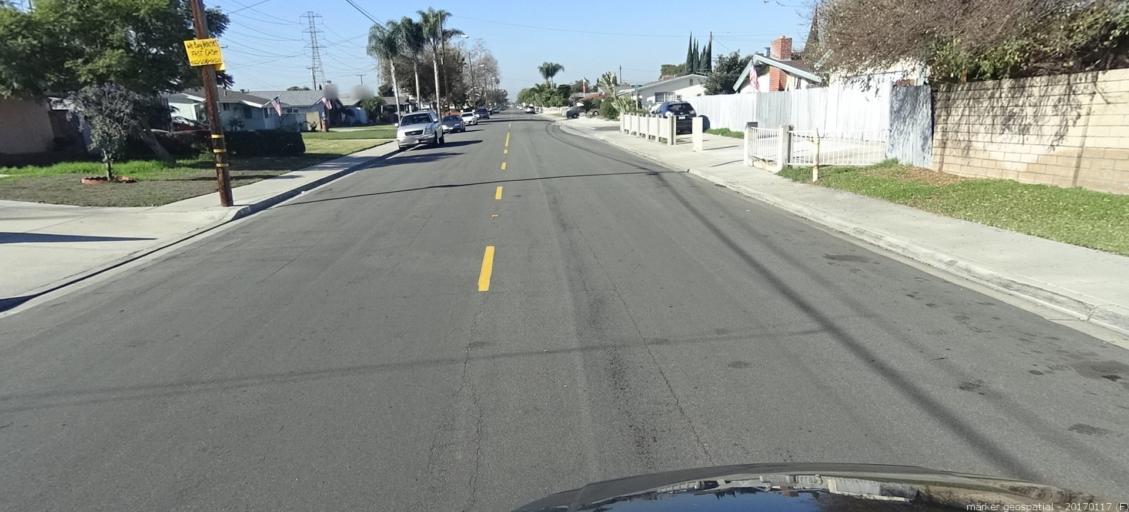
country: US
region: California
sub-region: Orange County
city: Stanton
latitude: 33.8078
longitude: -117.9611
